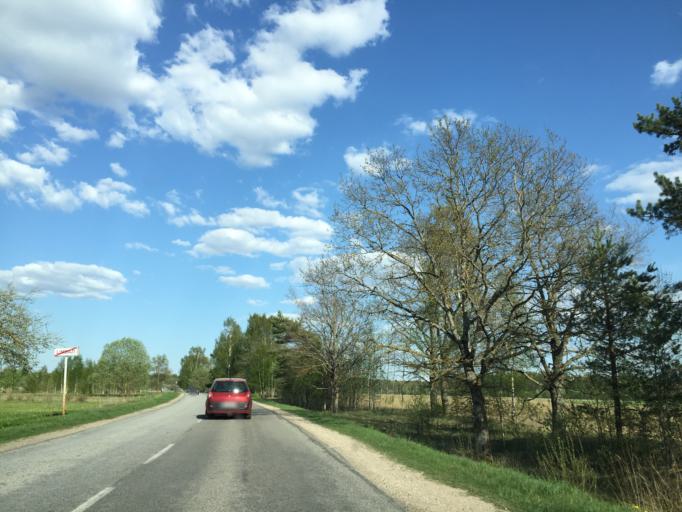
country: LV
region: Limbazu Rajons
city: Limbazi
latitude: 57.5115
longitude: 24.7404
